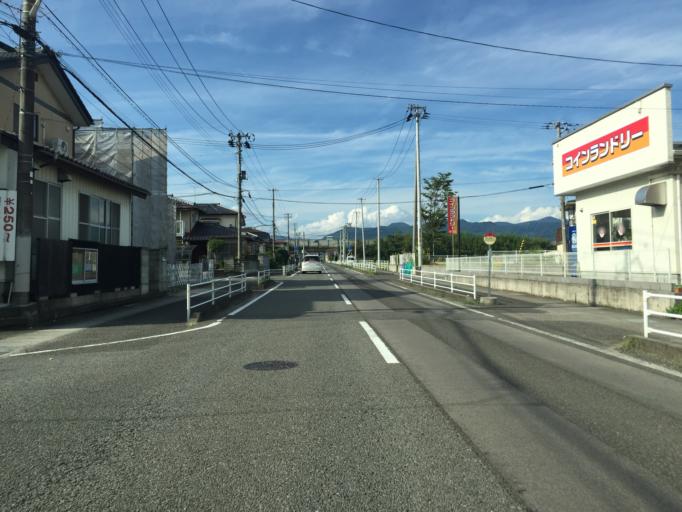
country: JP
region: Fukushima
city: Fukushima-shi
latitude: 37.8013
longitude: 140.4595
